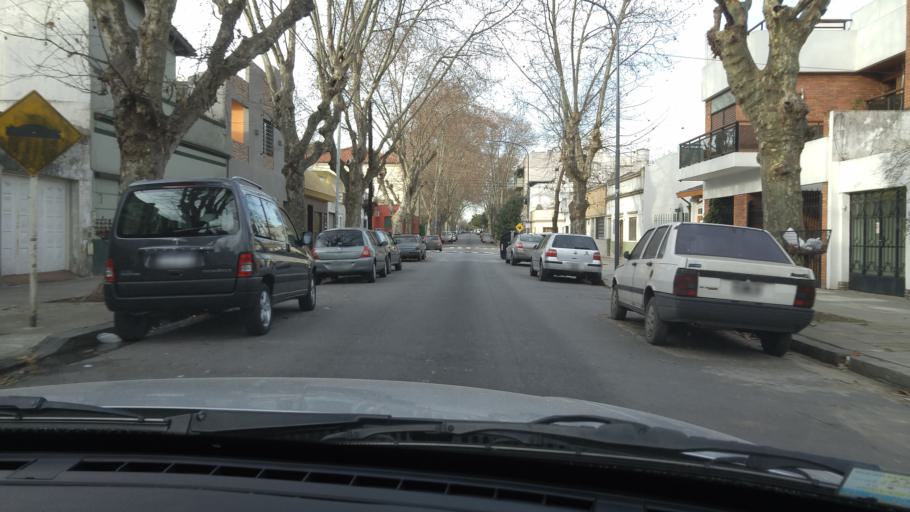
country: AR
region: Buenos Aires F.D.
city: Villa Santa Rita
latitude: -34.6297
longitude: -58.5233
